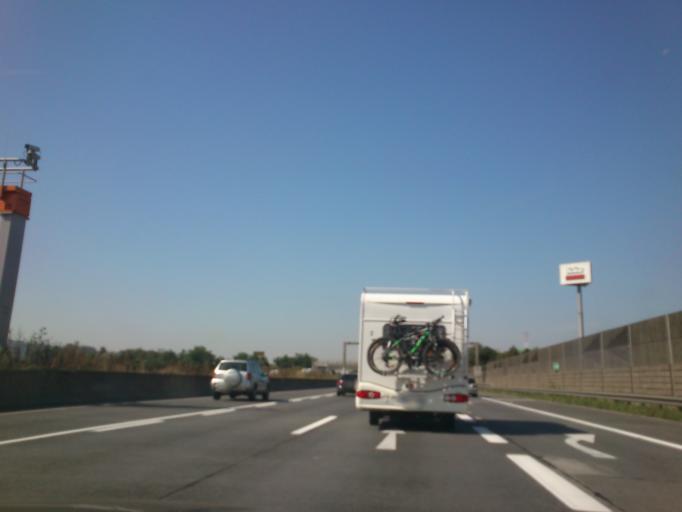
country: AT
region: Upper Austria
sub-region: Politischer Bezirk Linz-Land
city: Ansfelden
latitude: 48.2175
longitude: 14.2910
